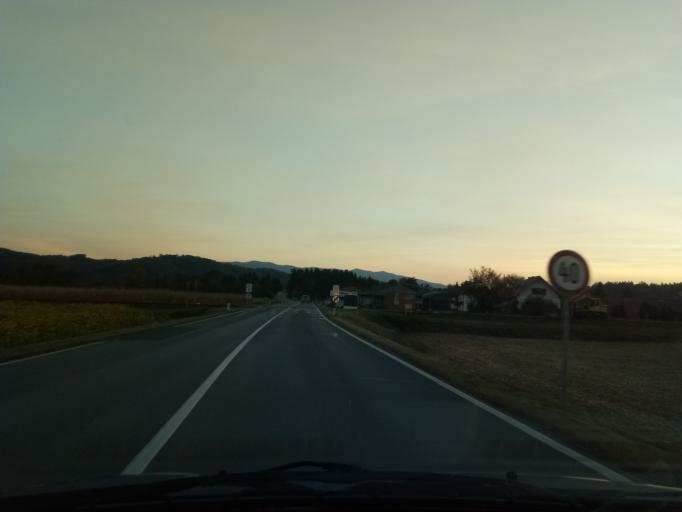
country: AT
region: Styria
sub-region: Politischer Bezirk Deutschlandsberg
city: Sankt Martin im Sulmtal
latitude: 46.7462
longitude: 15.3260
